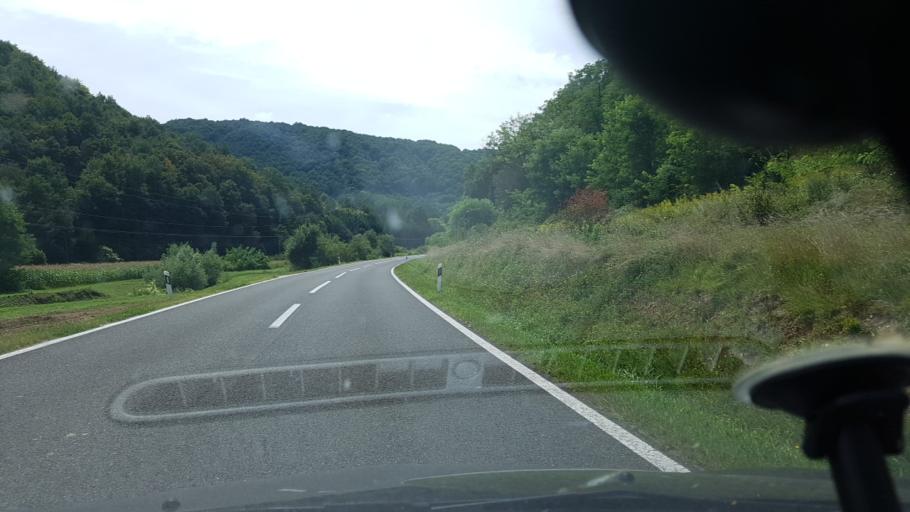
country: HR
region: Varazdinska
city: Lepoglava
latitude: 46.2141
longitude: 16.0038
